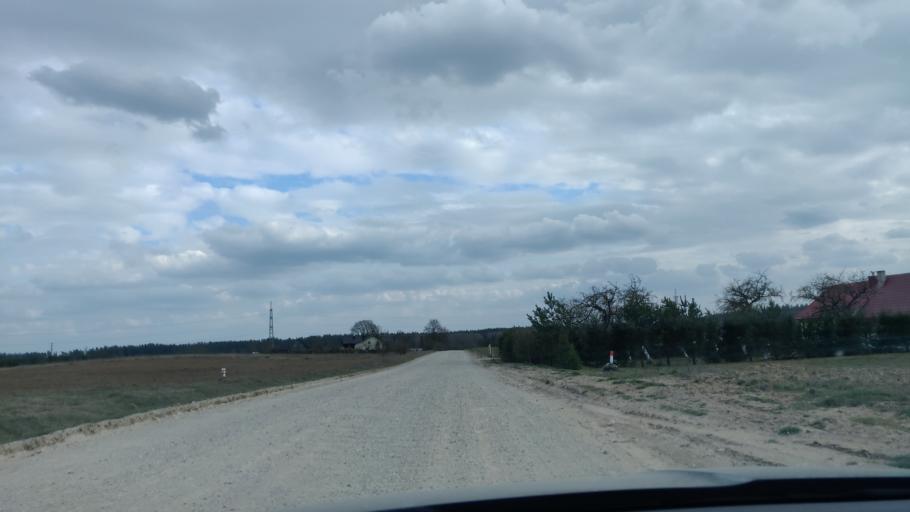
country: LT
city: Lentvaris
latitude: 54.6125
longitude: 25.0699
